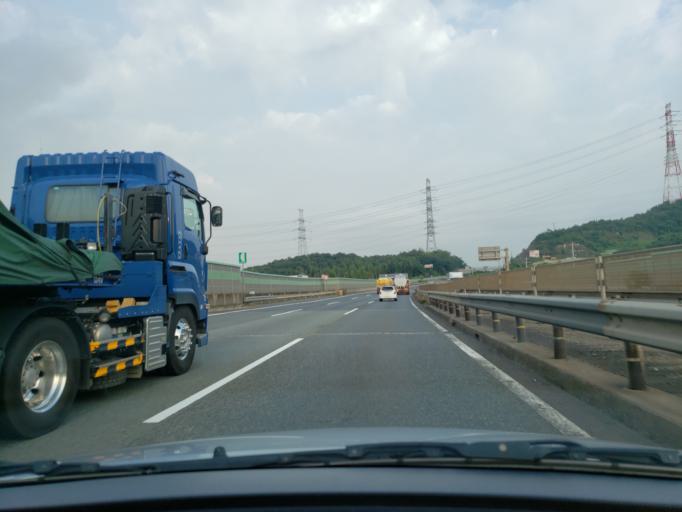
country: JP
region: Hyogo
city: Shirahamacho-usazakiminami
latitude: 34.7987
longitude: 134.7150
